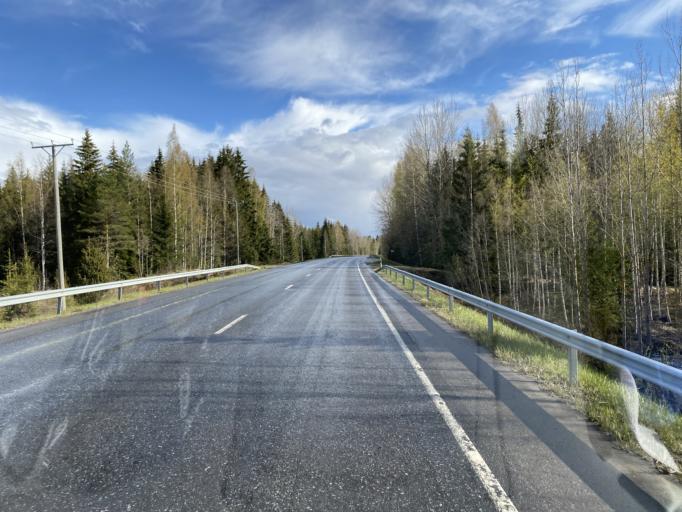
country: FI
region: Pirkanmaa
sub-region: Etelae-Pirkanmaa
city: Viiala
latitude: 61.2359
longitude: 23.7408
